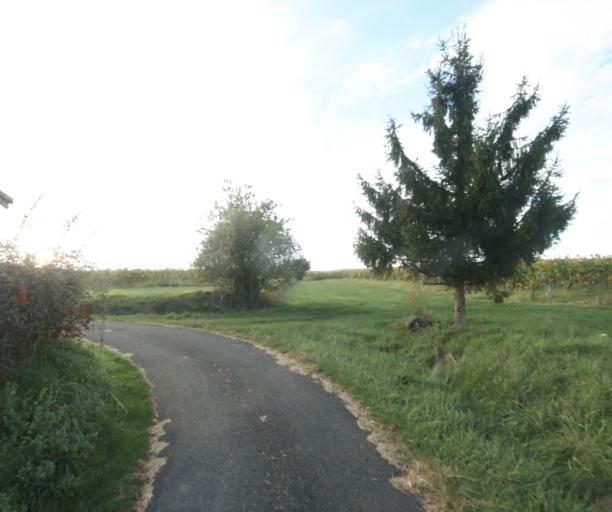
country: FR
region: Midi-Pyrenees
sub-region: Departement du Gers
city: Le Houga
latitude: 43.8509
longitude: -0.1260
